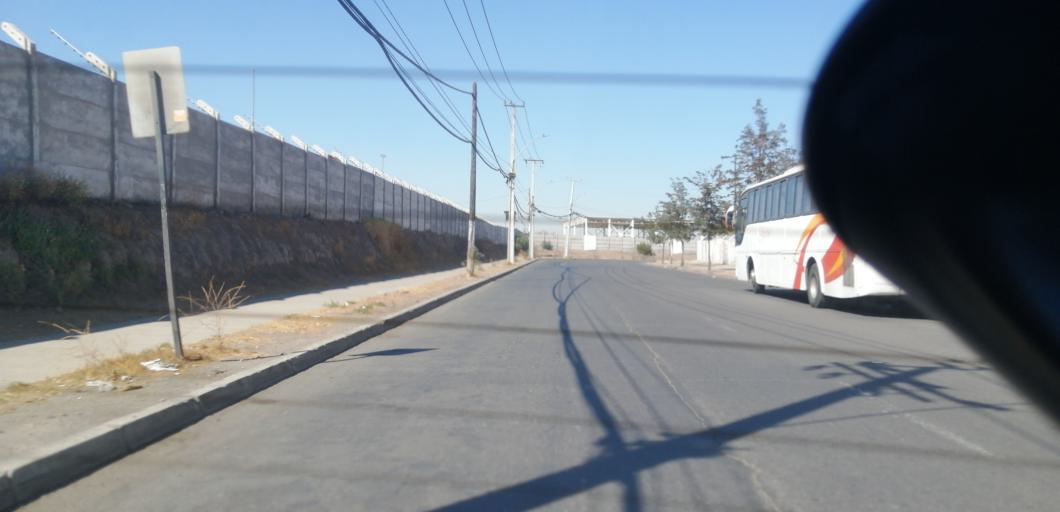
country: CL
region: Santiago Metropolitan
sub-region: Provincia de Santiago
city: Lo Prado
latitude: -33.4497
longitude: -70.7778
